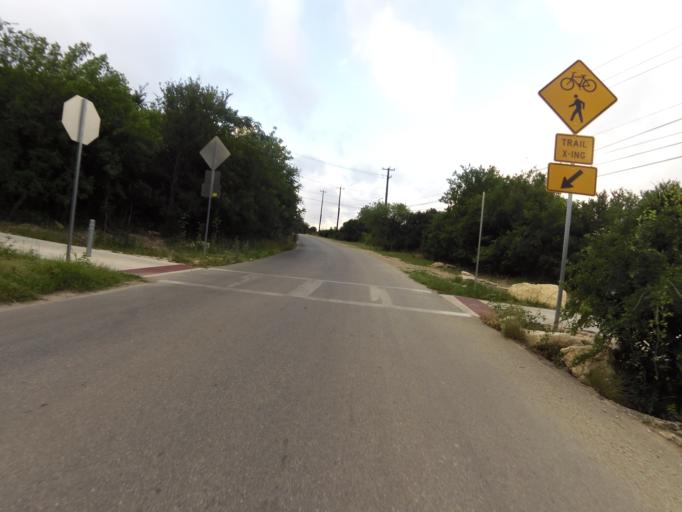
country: US
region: Texas
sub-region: Bexar County
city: Shavano Park
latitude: 29.5930
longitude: -98.6025
